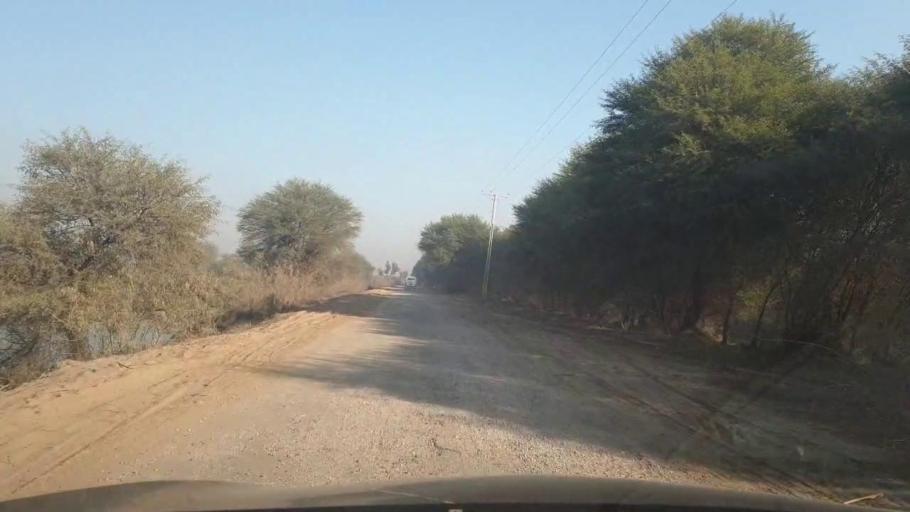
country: PK
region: Sindh
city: Mirpur Mathelo
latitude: 28.0636
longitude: 69.4647
